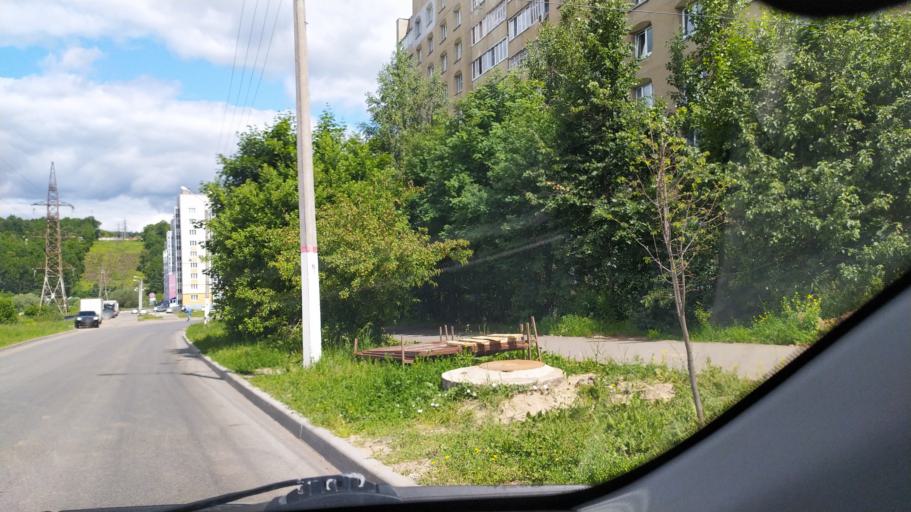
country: RU
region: Chuvashia
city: Novyye Lapsary
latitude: 56.1206
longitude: 47.1747
